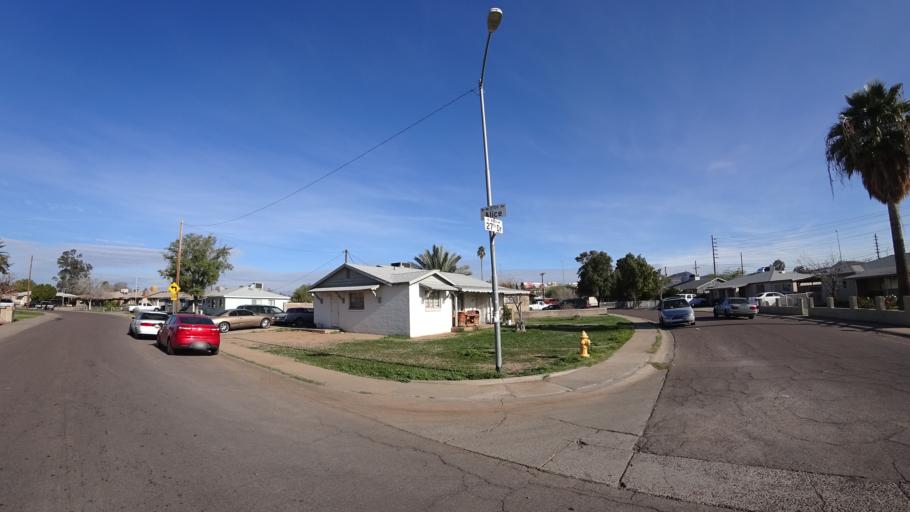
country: US
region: Arizona
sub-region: Maricopa County
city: Glendale
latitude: 33.5630
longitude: -112.1181
